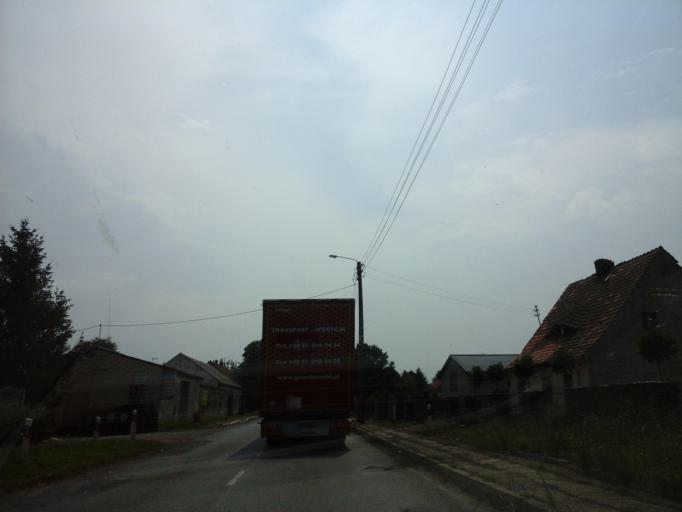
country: PL
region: Lower Silesian Voivodeship
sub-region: Powiat wroclawski
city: Zorawina
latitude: 50.9150
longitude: 17.0667
